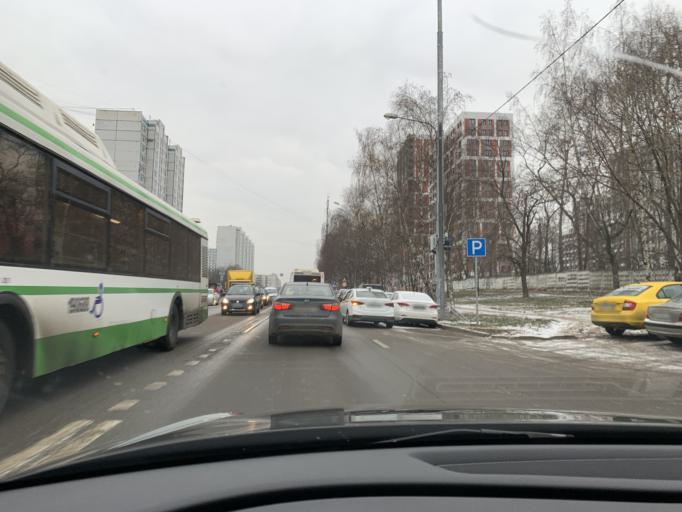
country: RU
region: Moscow
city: Zapadnoye Degunino
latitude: 55.8776
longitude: 37.5395
